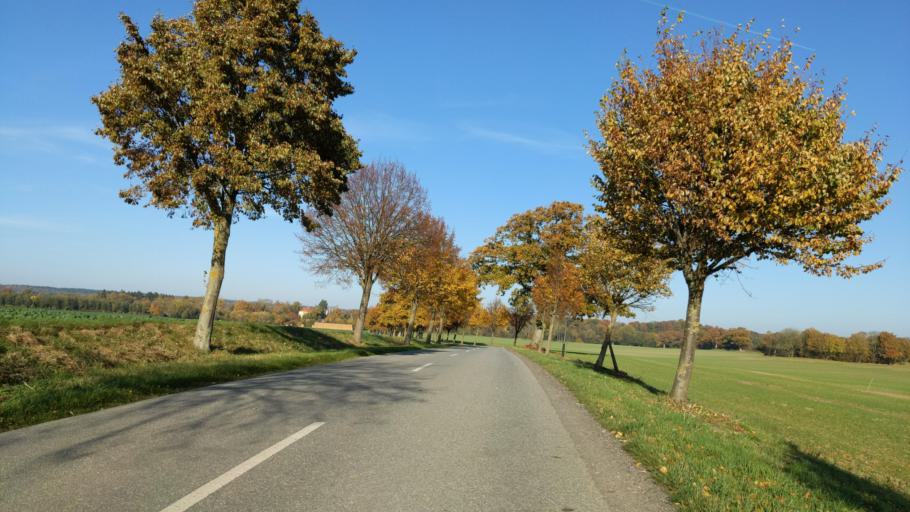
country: DE
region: Schleswig-Holstein
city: Neustadt in Holstein
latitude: 54.1213
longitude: 10.7797
